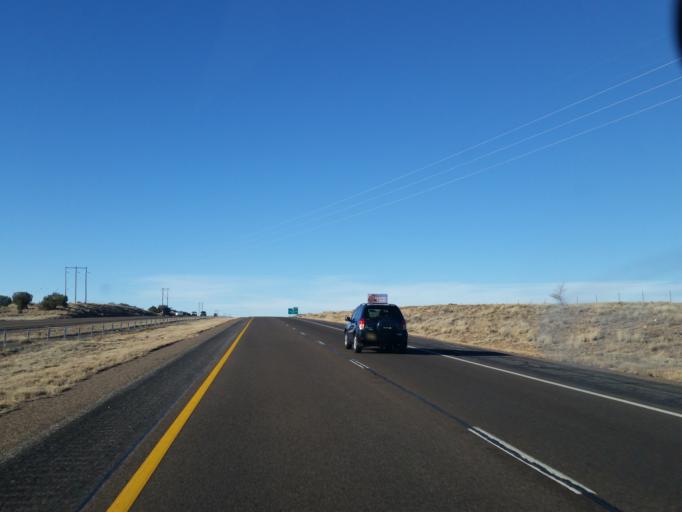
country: US
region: New Mexico
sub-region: Sandoval County
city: Santo Domingo Pueblo
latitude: 35.4807
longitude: -106.2793
